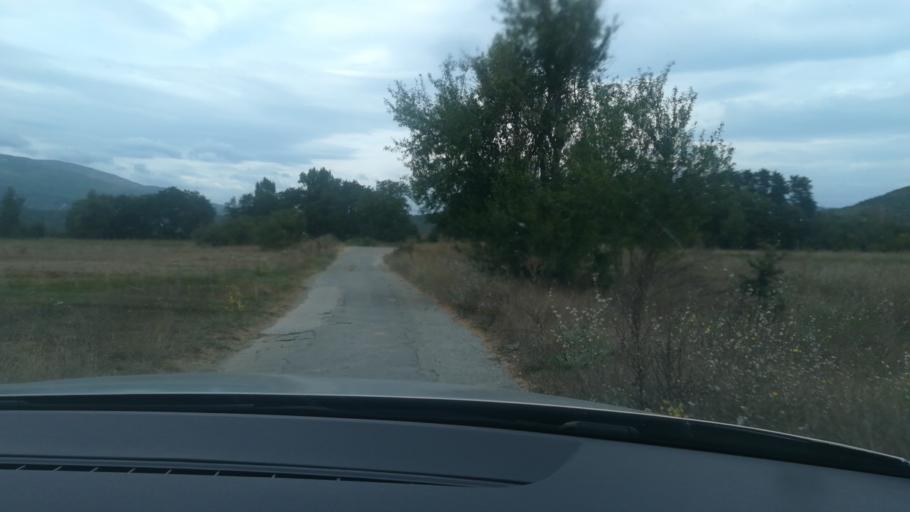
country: MK
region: Debarca
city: Belcista
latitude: 41.2968
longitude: 20.8312
